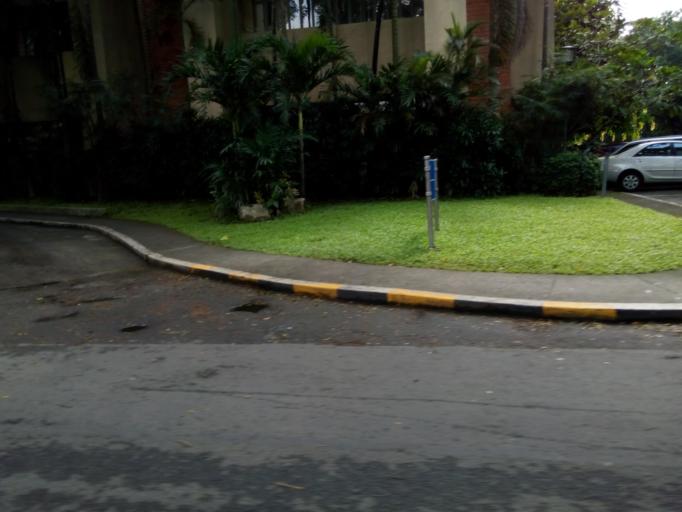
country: PH
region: Metro Manila
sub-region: Quezon City
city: Quezon City
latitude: 14.6545
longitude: 121.0732
